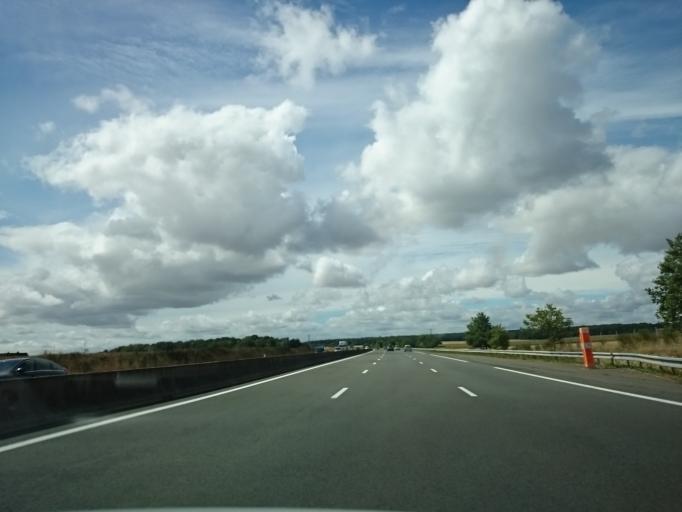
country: FR
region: Centre
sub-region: Departement d'Eure-et-Loir
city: Brou
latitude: 48.2768
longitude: 1.1845
